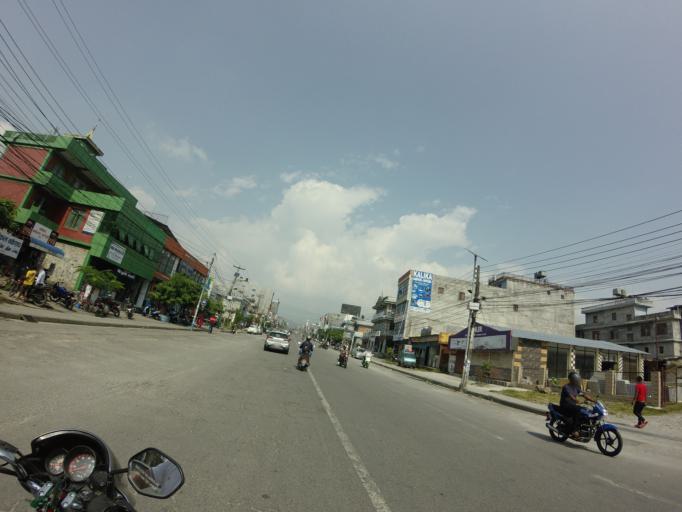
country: NP
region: Western Region
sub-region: Gandaki Zone
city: Pokhara
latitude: 28.2138
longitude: 83.9856
